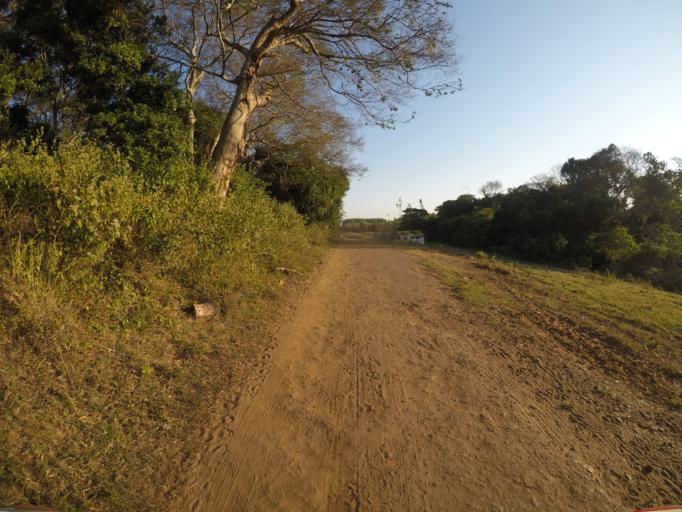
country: ZA
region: KwaZulu-Natal
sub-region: uThungulu District Municipality
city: KwaMbonambi
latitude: -28.6939
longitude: 32.1985
